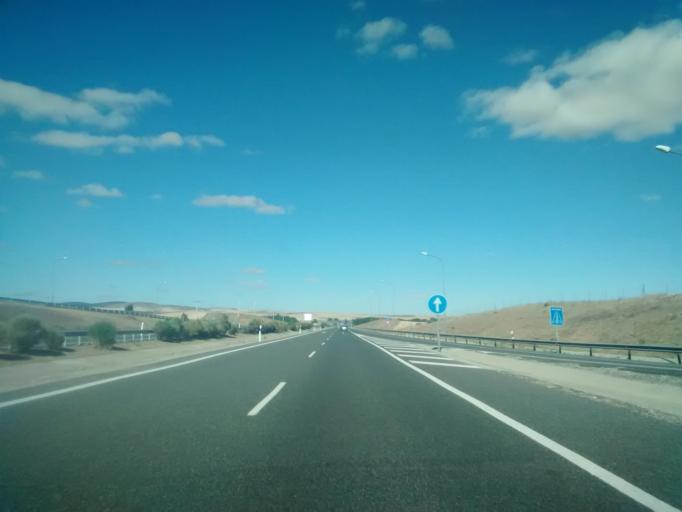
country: ES
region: Castille and Leon
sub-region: Provincia de Avila
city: San Pedro del Arroyo
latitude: 40.8096
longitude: -4.8497
